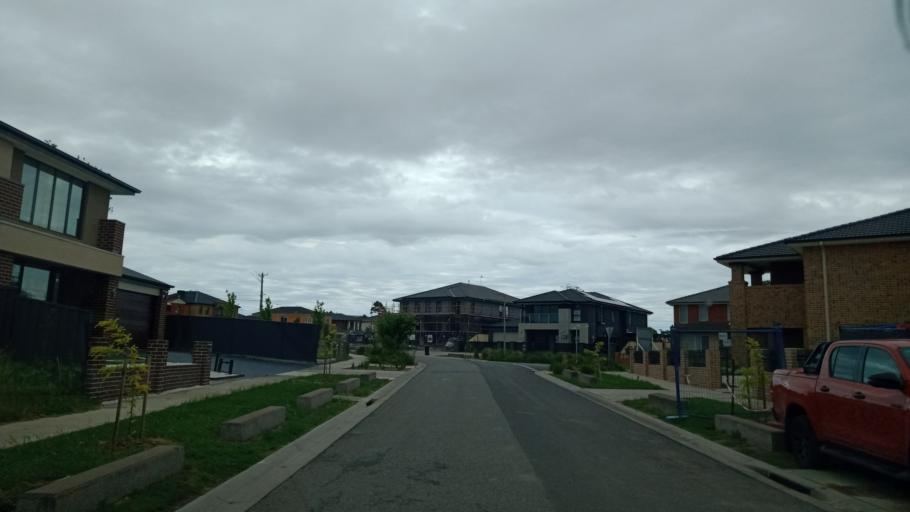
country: AU
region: Victoria
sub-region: Greater Dandenong
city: Springvale
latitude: -37.9499
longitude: 145.1598
